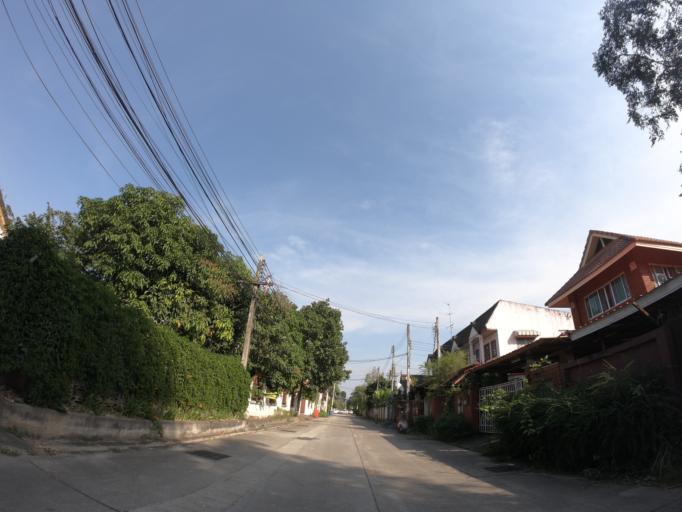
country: TH
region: Chiang Mai
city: Chiang Mai
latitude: 18.8180
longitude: 98.9911
